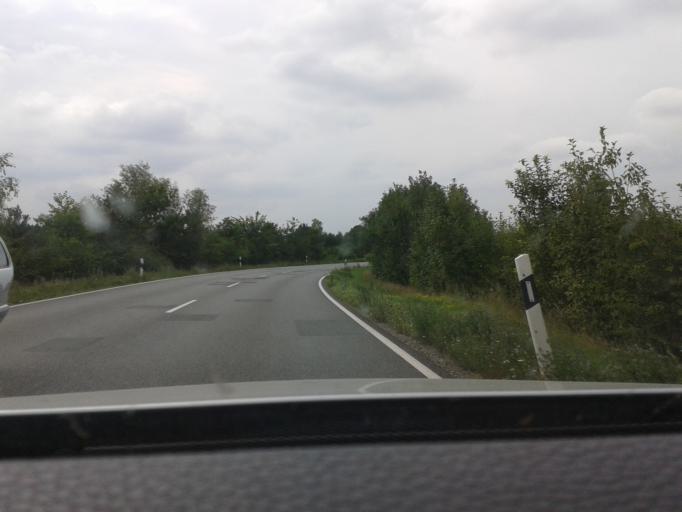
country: DE
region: Lower Saxony
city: Meinersen
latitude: 52.4800
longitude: 10.3432
